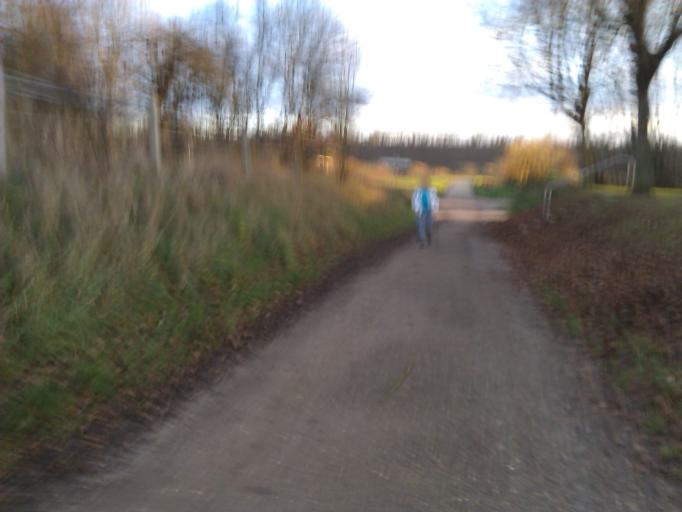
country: DE
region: Baden-Wuerttemberg
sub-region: Regierungsbezirk Stuttgart
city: Oedheim
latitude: 49.2357
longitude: 9.2287
